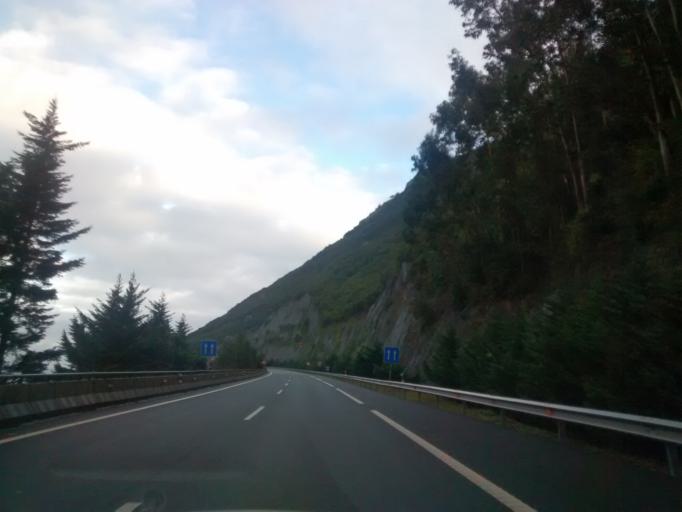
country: ES
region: Cantabria
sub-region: Provincia de Cantabria
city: Liendo
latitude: 43.3921
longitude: -3.3132
